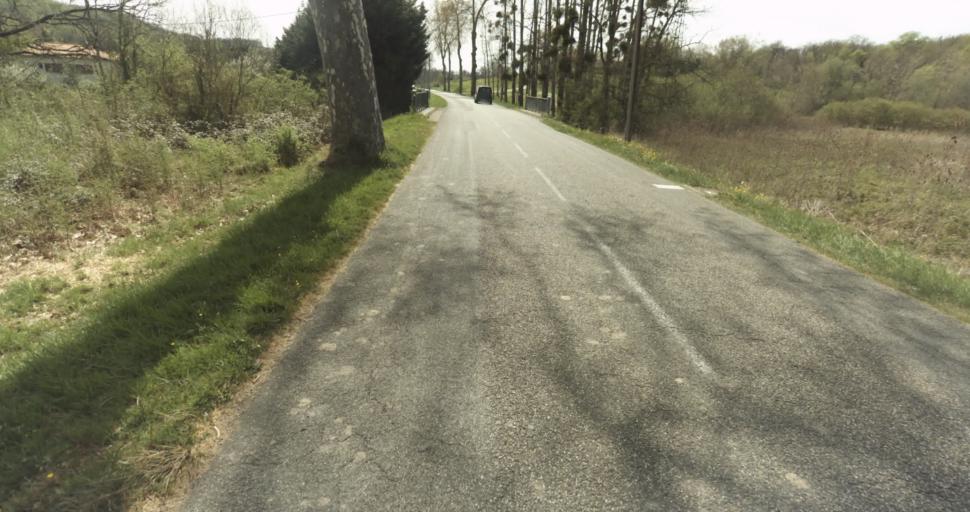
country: FR
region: Midi-Pyrenees
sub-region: Departement du Tarn-et-Garonne
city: Moissac
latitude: 44.1576
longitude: 1.1115
